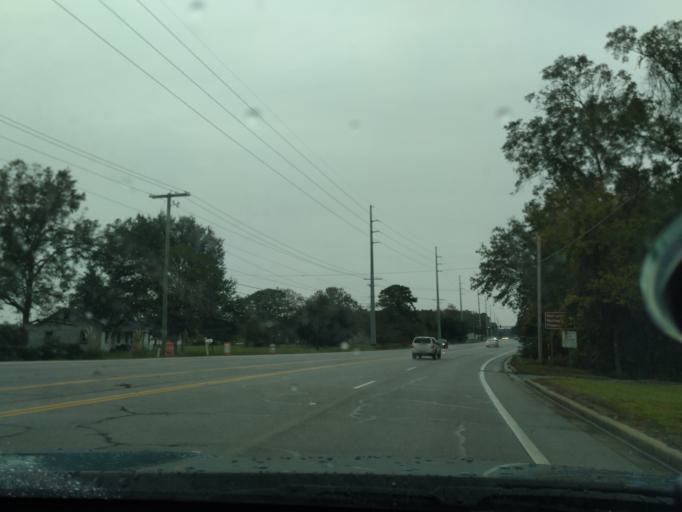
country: US
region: South Carolina
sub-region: Charleston County
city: Folly Beach
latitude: 32.6991
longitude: -79.9678
